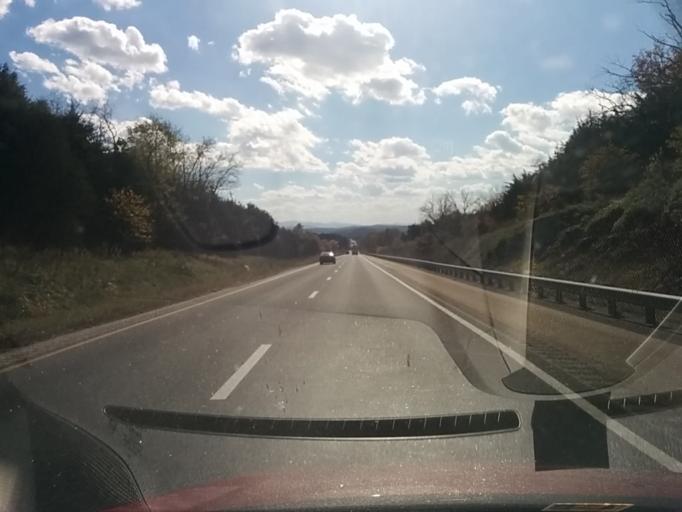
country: US
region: Virginia
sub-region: Rockbridge County
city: East Lexington
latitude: 37.8281
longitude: -79.3749
